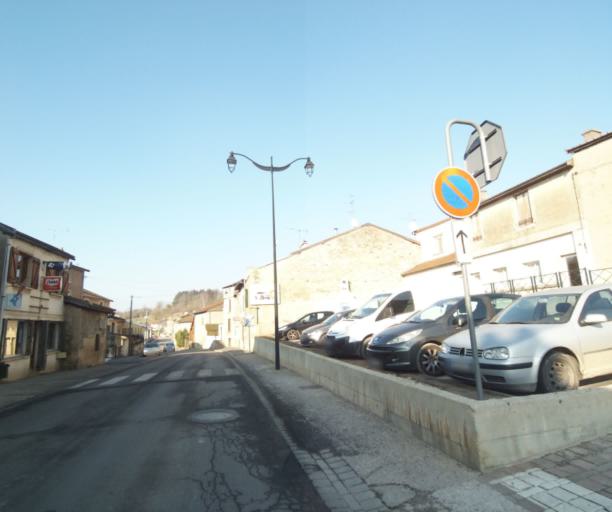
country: FR
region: Champagne-Ardenne
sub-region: Departement de la Haute-Marne
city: Wassy
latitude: 48.4915
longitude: 4.9673
